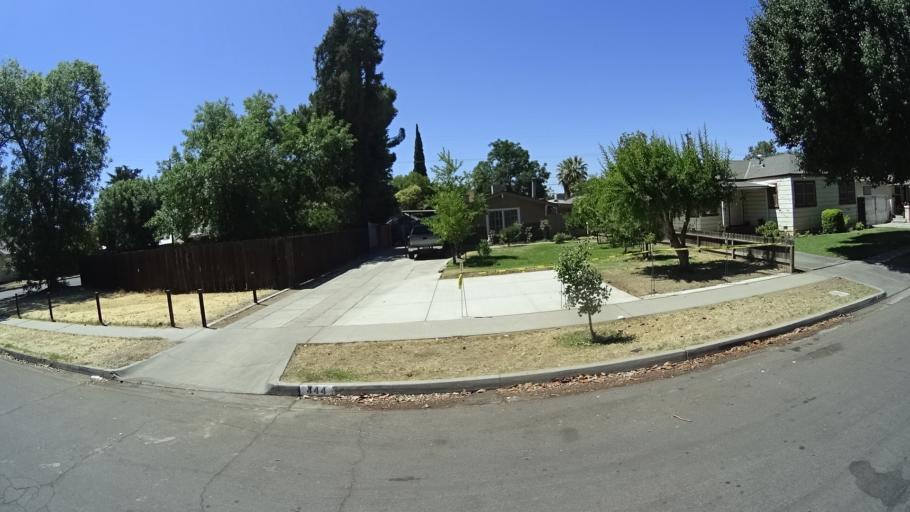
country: US
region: California
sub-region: Fresno County
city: Fresno
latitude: 36.7813
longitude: -119.8066
